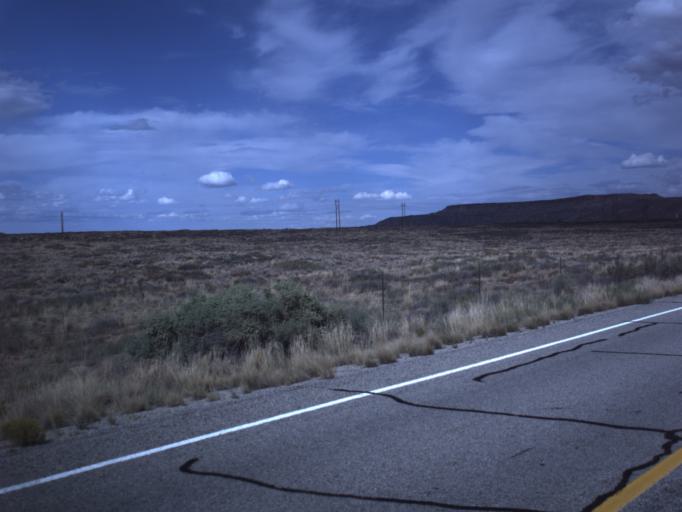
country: US
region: Utah
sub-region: San Juan County
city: Blanding
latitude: 37.2964
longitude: -109.4800
